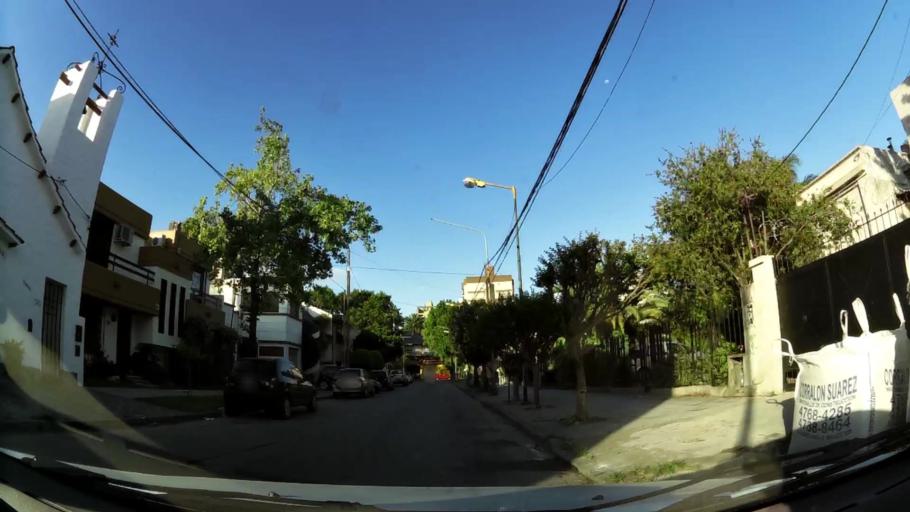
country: AR
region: Buenos Aires
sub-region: Partido de General San Martin
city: General San Martin
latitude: -34.5558
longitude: -58.5591
